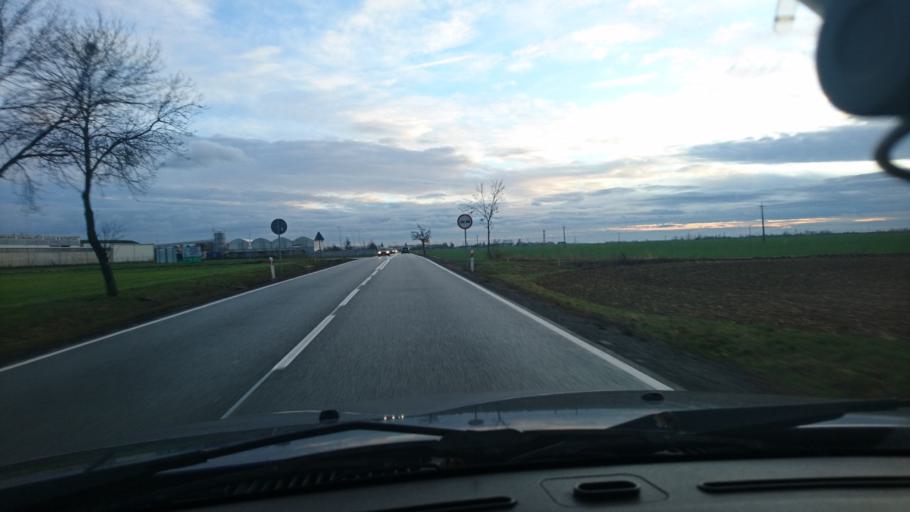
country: PL
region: Opole Voivodeship
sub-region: Powiat kluczborski
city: Kluczbork
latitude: 51.0049
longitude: 18.2048
